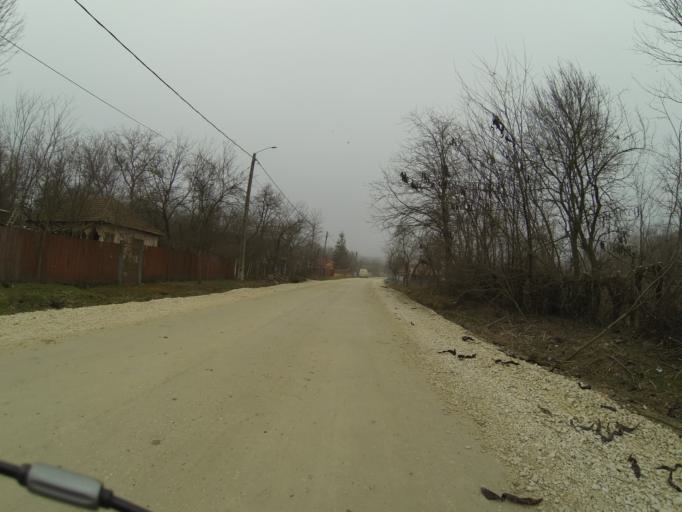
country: RO
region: Mehedinti
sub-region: Comuna Balacita
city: Gvardinita
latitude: 44.4060
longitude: 23.1439
